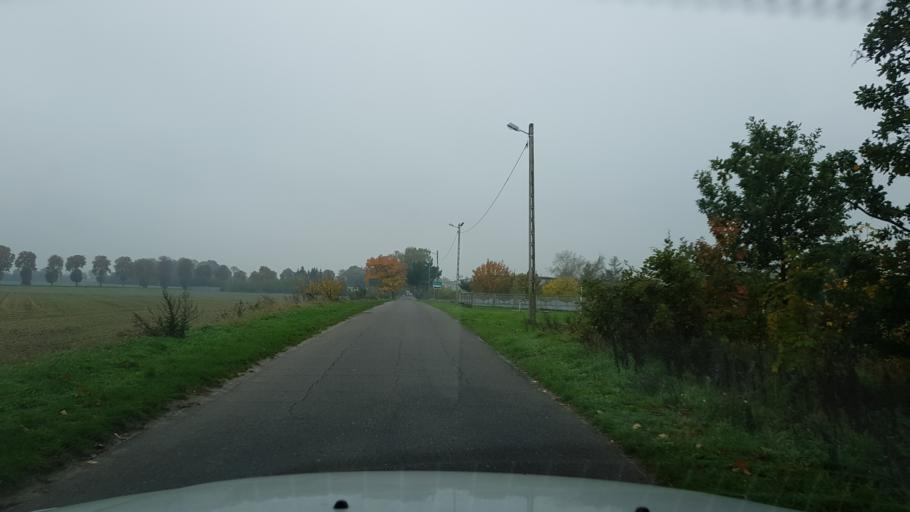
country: PL
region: West Pomeranian Voivodeship
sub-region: Powiat stargardzki
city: Dolice
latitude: 53.1535
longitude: 15.2388
